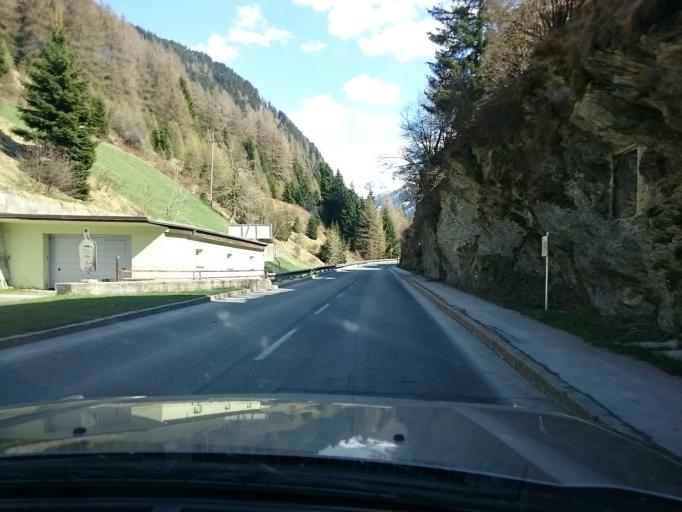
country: AT
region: Tyrol
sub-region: Politischer Bezirk Innsbruck Land
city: Gries am Brenner
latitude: 47.0351
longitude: 11.4827
